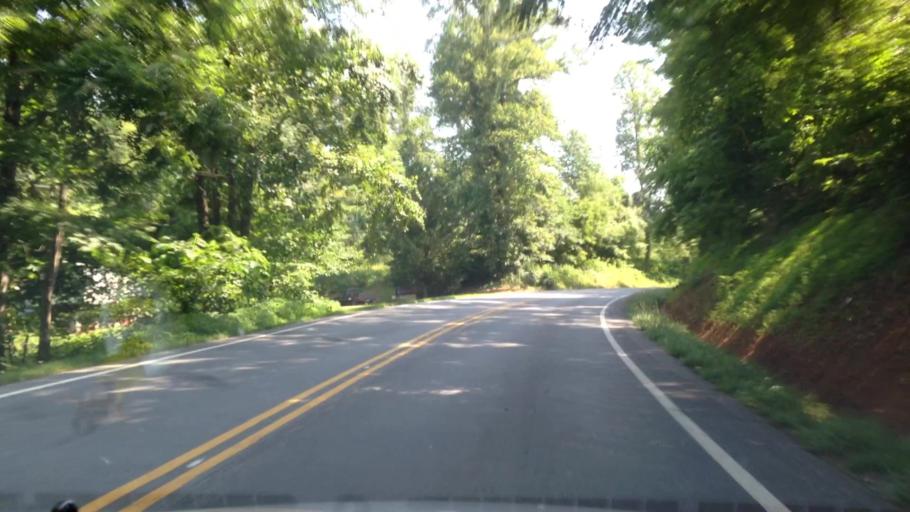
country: US
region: Virginia
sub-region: Patrick County
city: Stuart
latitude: 36.5885
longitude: -80.3299
